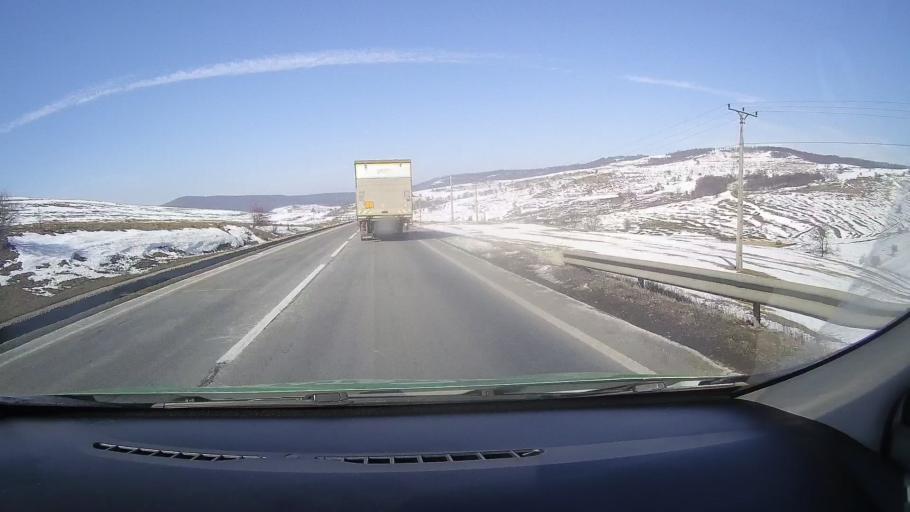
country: RO
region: Brasov
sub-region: Oras Rupea
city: Fiser
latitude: 46.0931
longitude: 25.1172
